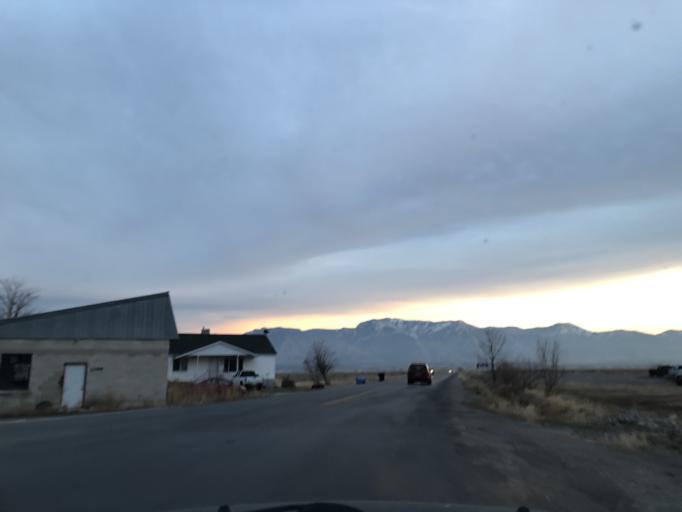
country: US
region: Utah
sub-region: Cache County
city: Benson
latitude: 41.7947
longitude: -111.8918
